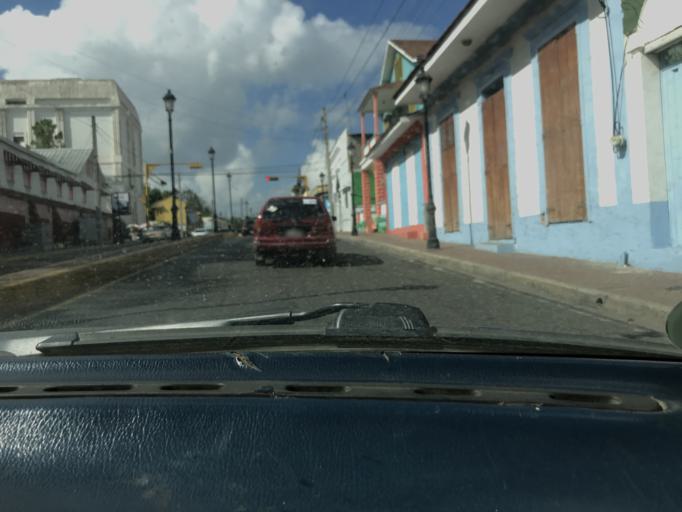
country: DO
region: Santiago
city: Santiago de los Caballeros
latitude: 19.4520
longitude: -70.7076
